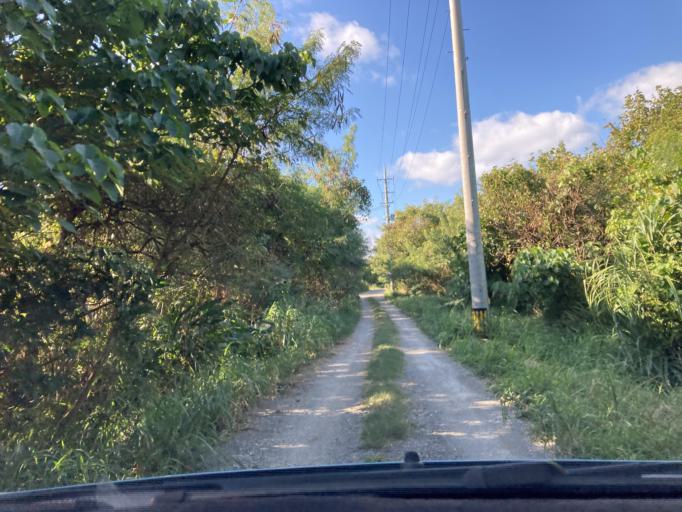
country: JP
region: Okinawa
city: Katsuren-haebaru
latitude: 26.3175
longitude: 127.9267
